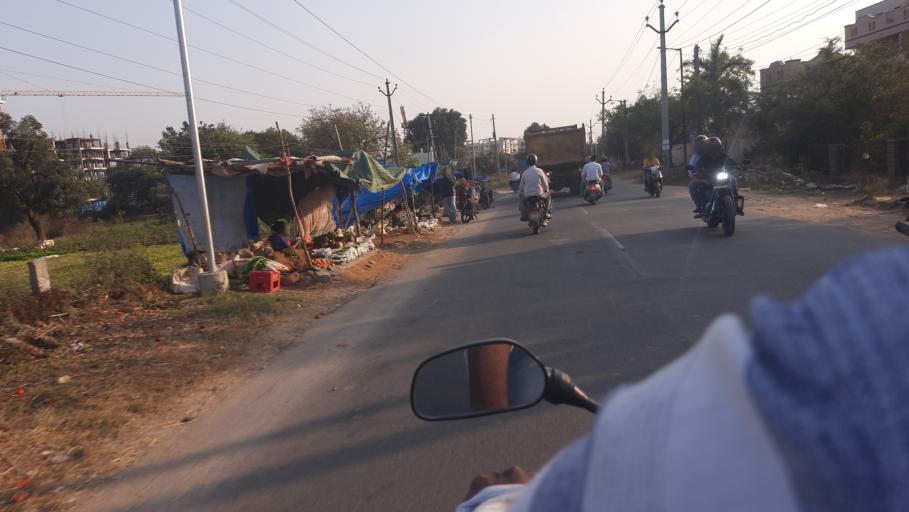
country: IN
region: Telangana
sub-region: Rangareddi
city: Secunderabad
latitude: 17.5240
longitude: 78.5416
